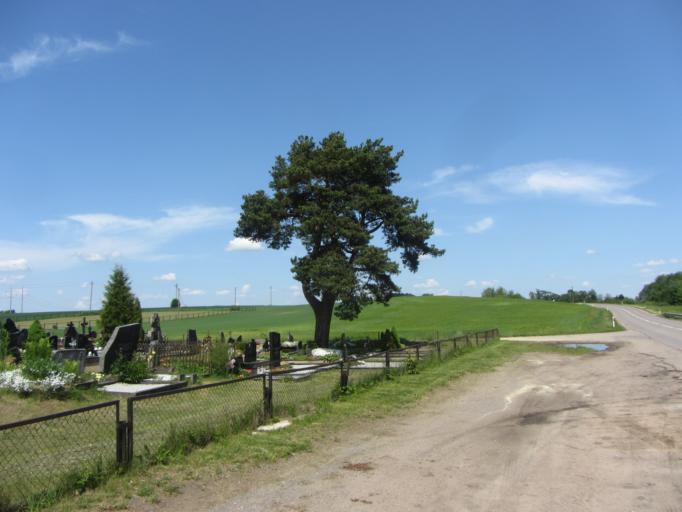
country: LT
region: Vilnius County
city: Elektrenai
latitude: 54.8915
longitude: 24.5913
